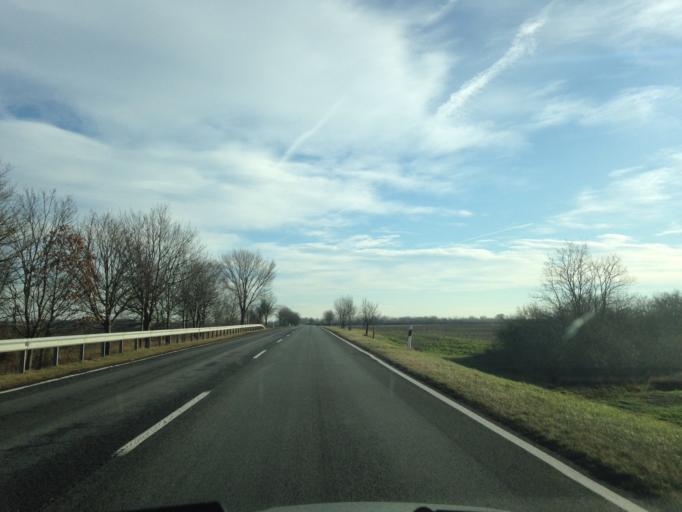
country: HU
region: Gyor-Moson-Sopron
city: Kimle
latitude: 47.7975
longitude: 17.3909
